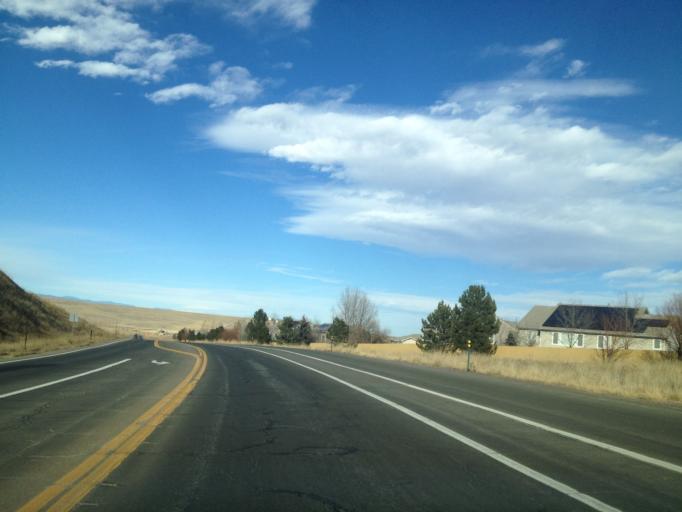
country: US
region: Colorado
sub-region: Boulder County
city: Superior
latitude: 39.9177
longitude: -105.1637
